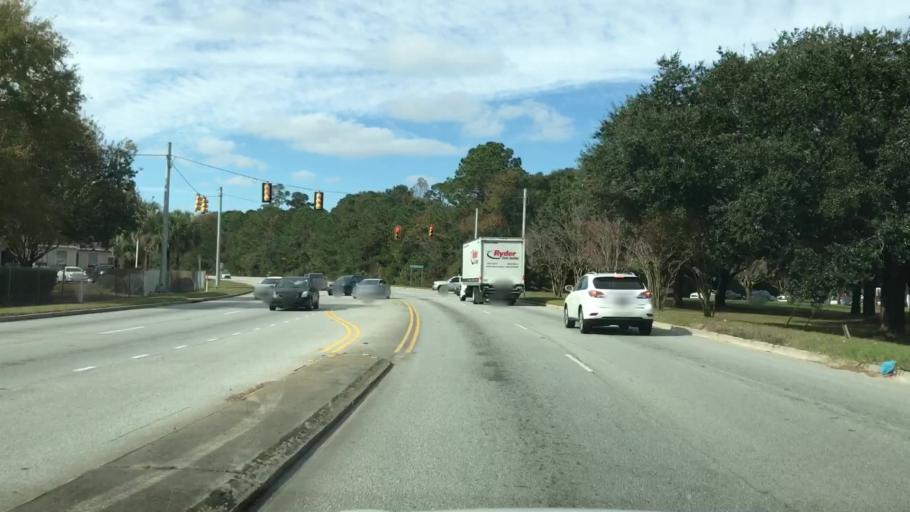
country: US
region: South Carolina
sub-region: Charleston County
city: North Charleston
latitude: 32.8072
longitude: -80.0235
